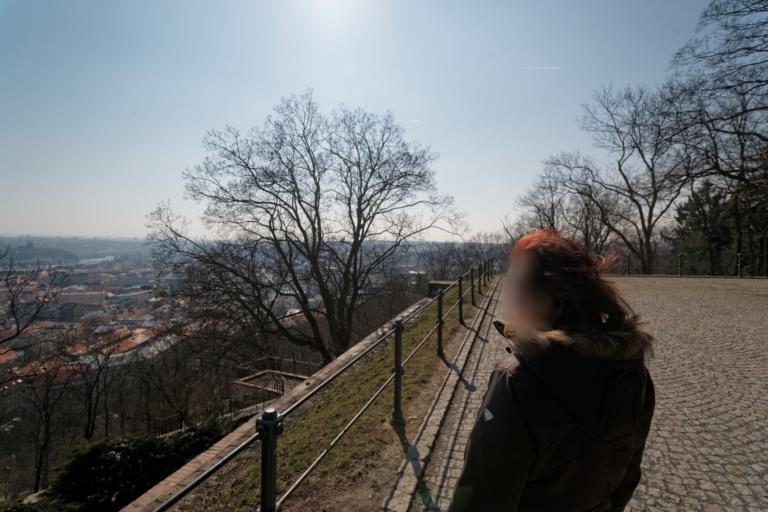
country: CZ
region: Praha
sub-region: Praha 1
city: Mala Strana
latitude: 50.0801
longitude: 14.4010
